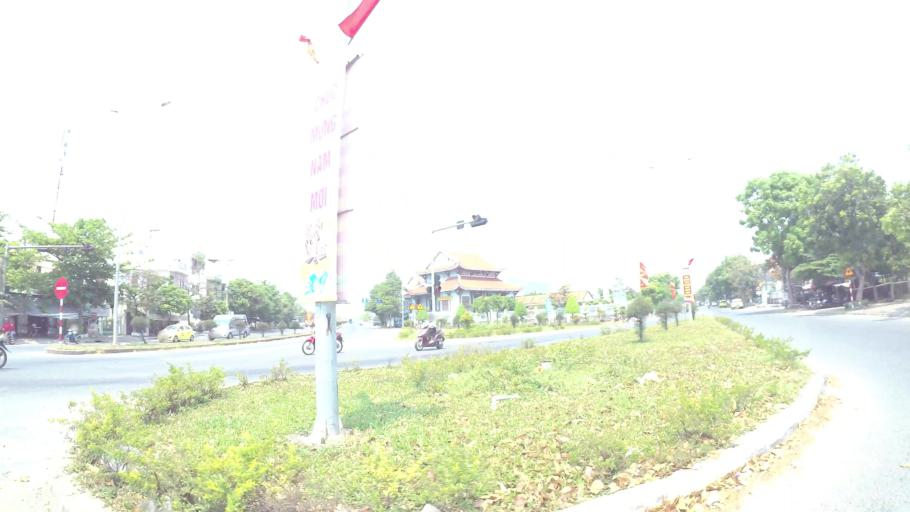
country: VN
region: Da Nang
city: Cam Le
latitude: 15.9805
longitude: 108.2082
